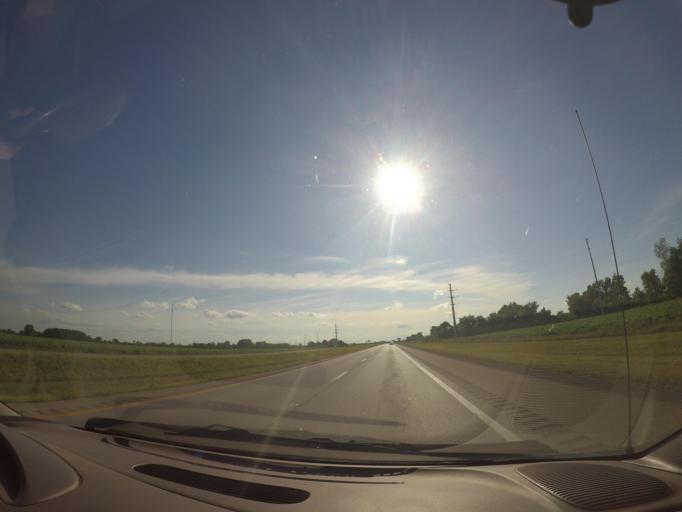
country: US
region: Ohio
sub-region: Henry County
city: Napoleon
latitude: 41.4170
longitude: -84.0803
